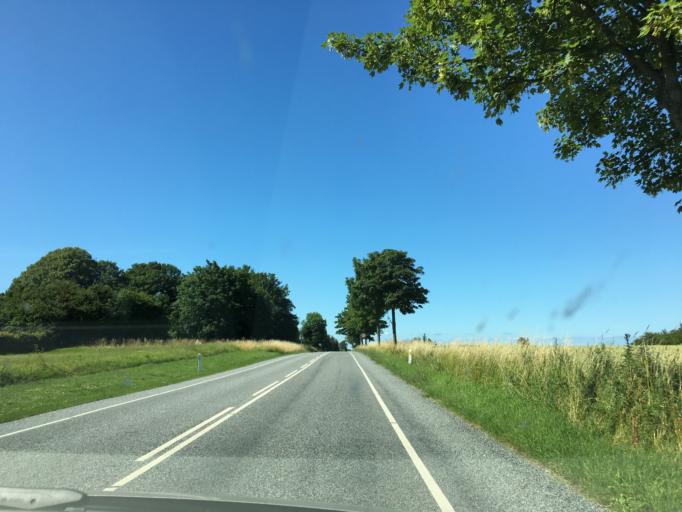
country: DK
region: South Denmark
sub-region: Langeland Kommune
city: Rudkobing
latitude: 54.7714
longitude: 10.7164
